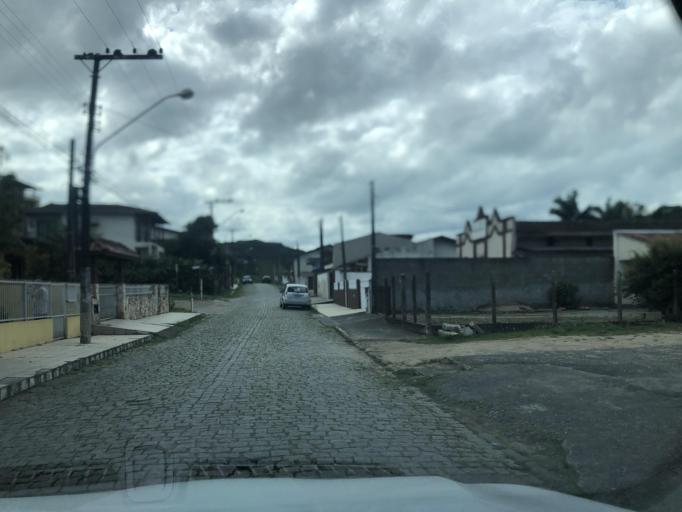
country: BR
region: Santa Catarina
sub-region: Sao Francisco Do Sul
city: Sao Francisco do Sul
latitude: -26.2478
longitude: -48.6291
